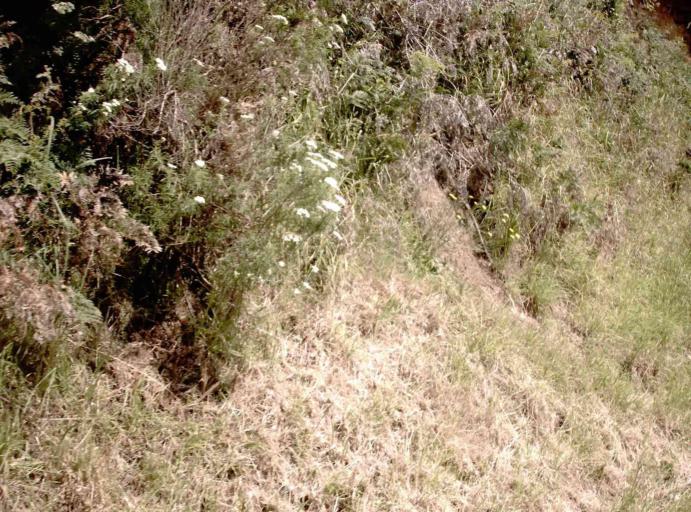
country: AU
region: Victoria
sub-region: Latrobe
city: Traralgon
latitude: -38.3444
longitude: 146.5704
